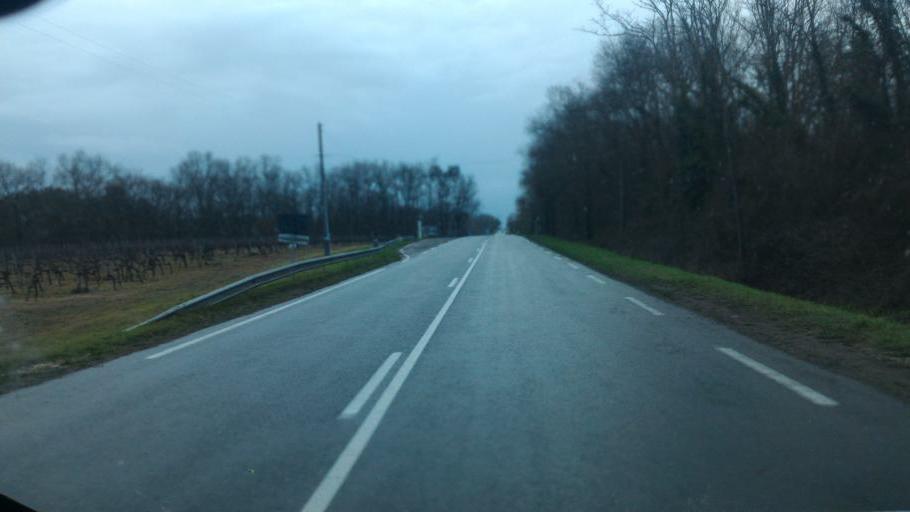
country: FR
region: Aquitaine
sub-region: Departement de la Gironde
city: Marcamps
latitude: 45.0440
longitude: -0.4672
